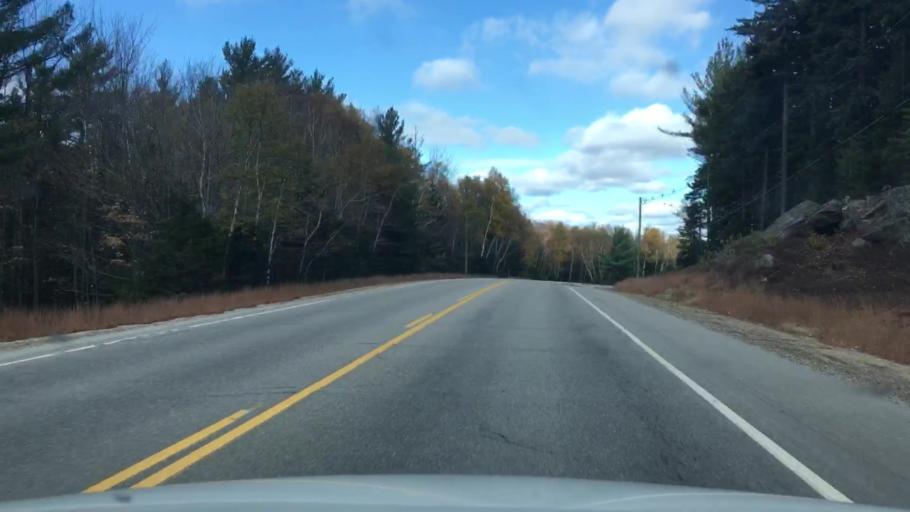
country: US
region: New Hampshire
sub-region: Coos County
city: Gorham
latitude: 44.2974
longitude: -71.2244
